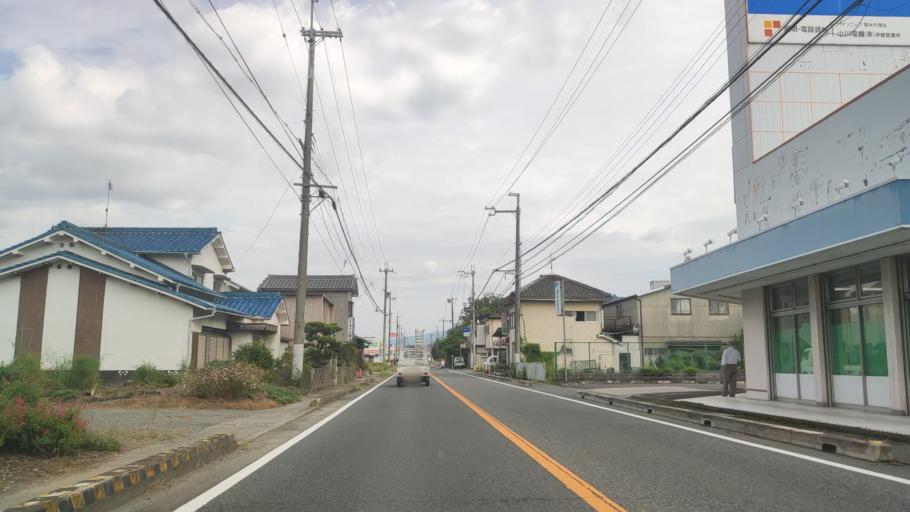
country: JP
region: Wakayama
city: Hashimoto
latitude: 34.2981
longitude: 135.5121
